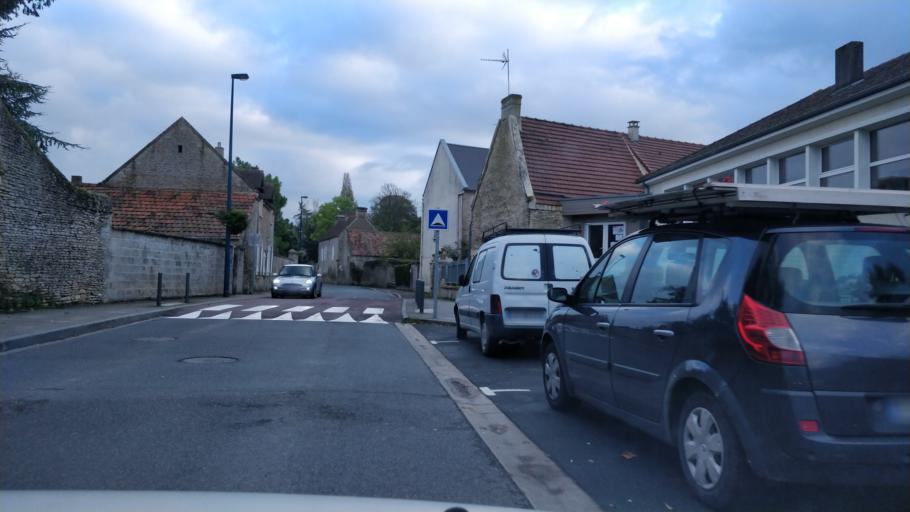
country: FR
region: Lower Normandy
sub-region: Departement du Calvados
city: Benouville
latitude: 49.2605
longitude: -0.2866
